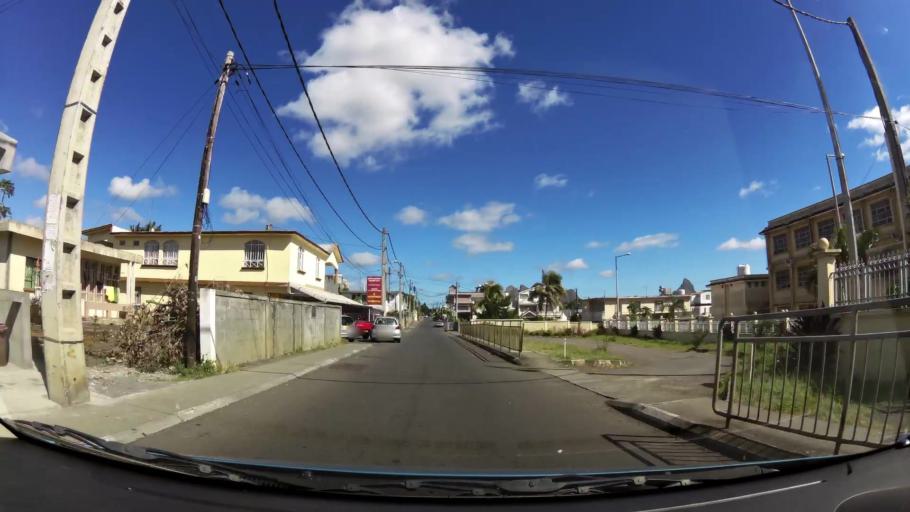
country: MU
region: Plaines Wilhems
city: Vacoas
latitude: -20.2859
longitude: 57.4793
